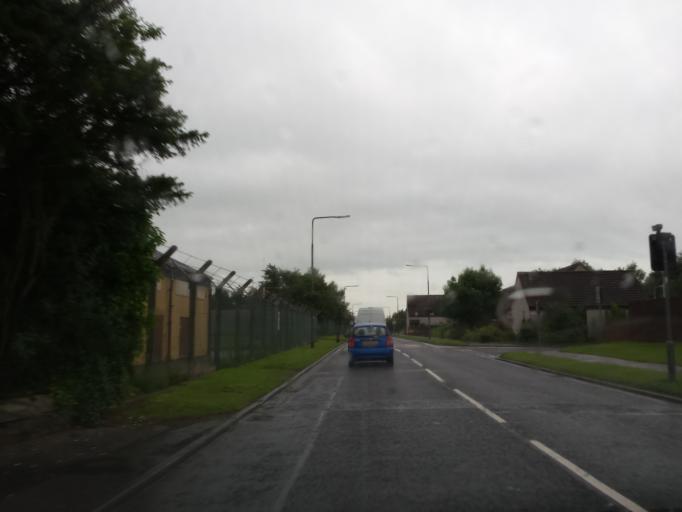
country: GB
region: Scotland
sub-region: Fife
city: Leuchars
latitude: 56.3807
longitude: -2.8884
